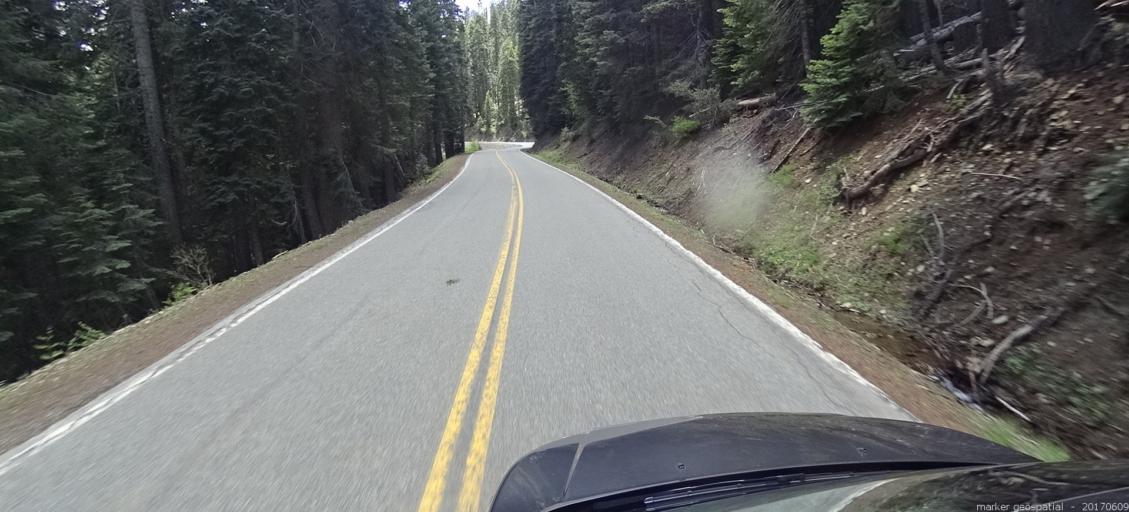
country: US
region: California
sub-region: Siskiyou County
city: Yreka
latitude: 41.4018
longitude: -122.9943
